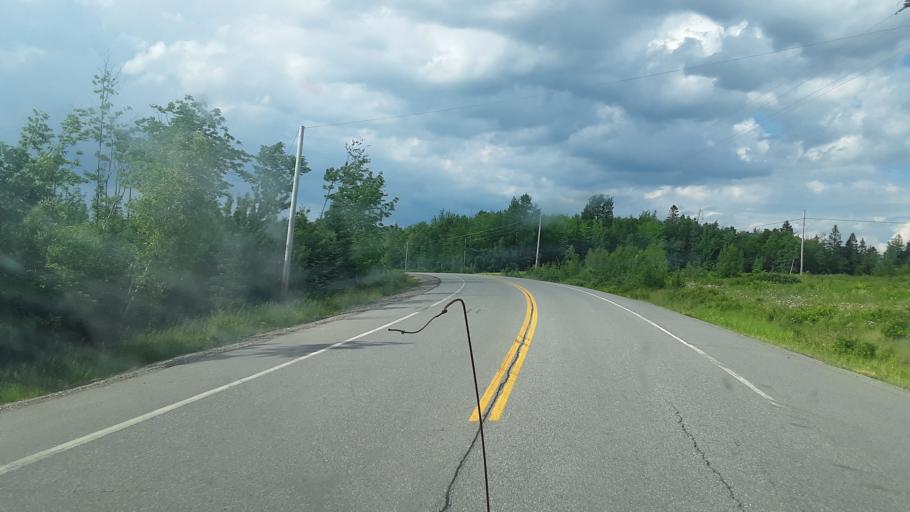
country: US
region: Maine
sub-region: Washington County
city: Machias
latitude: 45.0019
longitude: -67.5533
